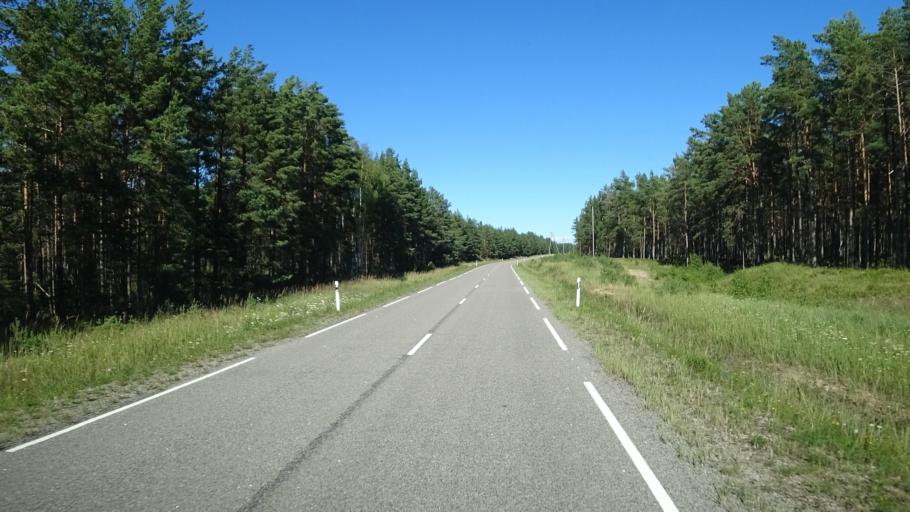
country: LV
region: Dundaga
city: Dundaga
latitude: 57.6786
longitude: 22.3495
